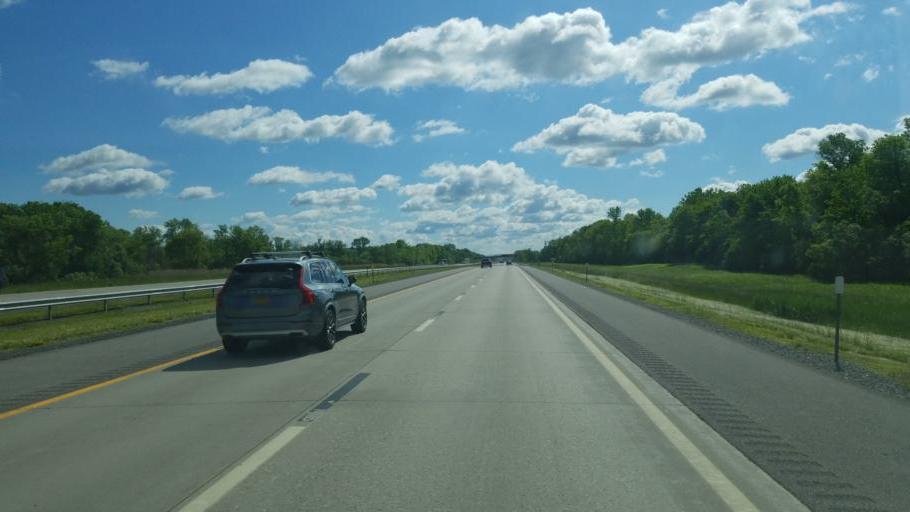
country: US
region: New York
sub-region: Onondaga County
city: Jordan
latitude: 43.0750
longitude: -76.4931
